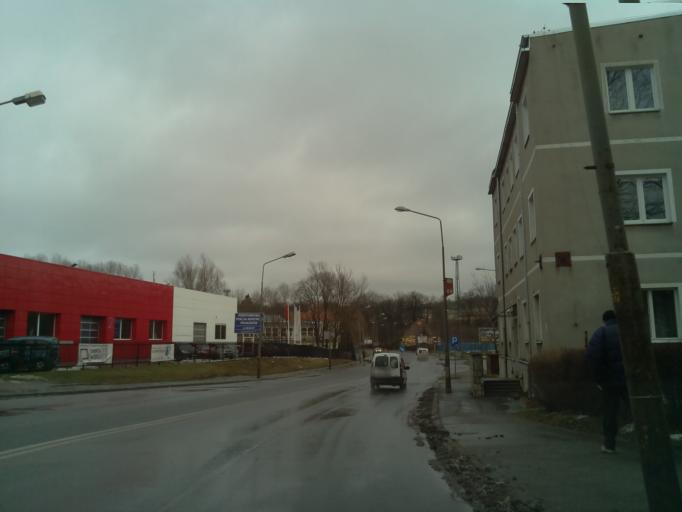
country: PL
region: Lower Silesian Voivodeship
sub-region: Powiat walbrzyski
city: Szczawno-Zdroj
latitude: 50.8123
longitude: 16.2966
